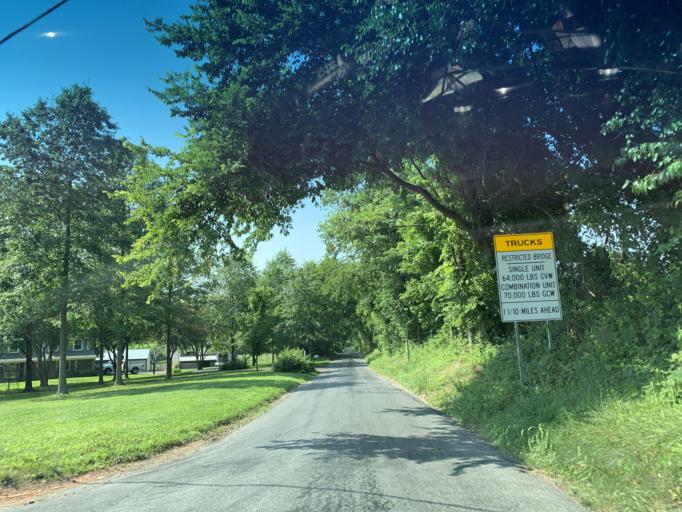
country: US
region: Maryland
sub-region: Montgomery County
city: Poolesville
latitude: 39.1339
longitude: -77.4485
